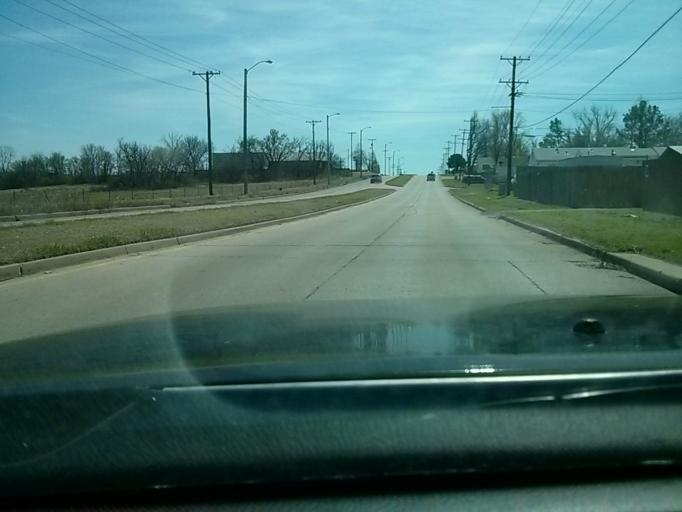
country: US
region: Oklahoma
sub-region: Tulsa County
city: Owasso
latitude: 36.1684
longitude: -95.8867
